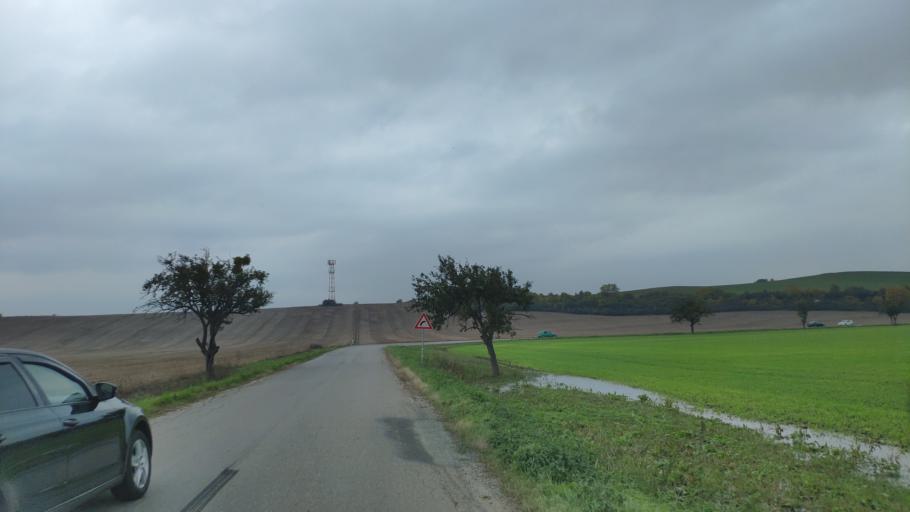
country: SK
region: Kosicky
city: Kosice
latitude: 48.6388
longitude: 21.3745
